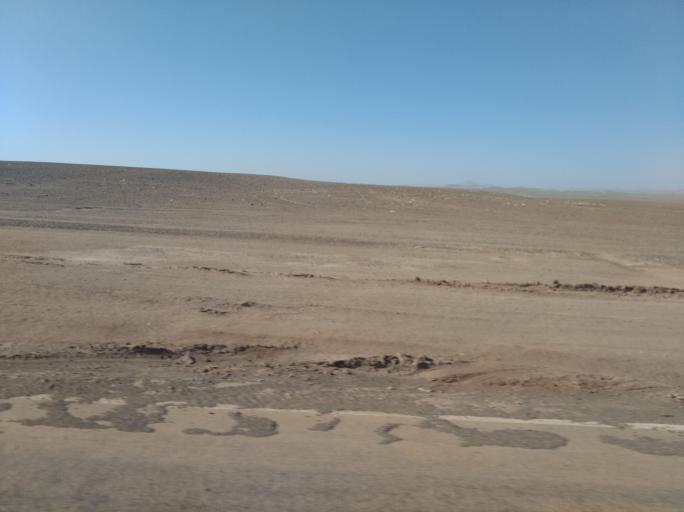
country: CL
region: Atacama
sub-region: Provincia de Copiapo
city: Copiapo
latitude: -27.3231
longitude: -70.8113
